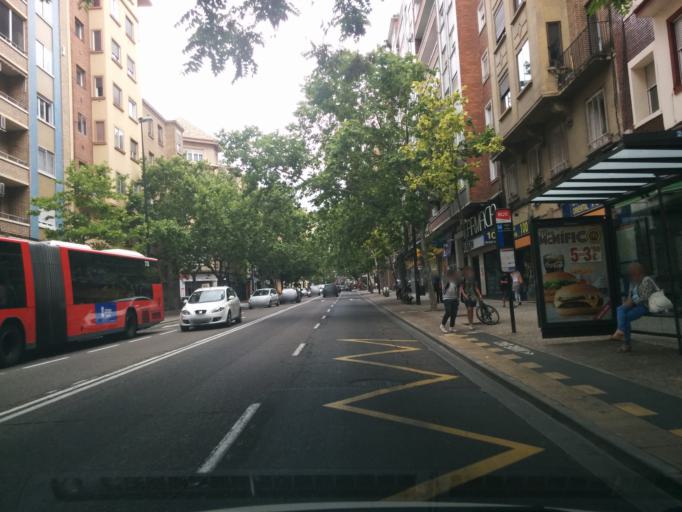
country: ES
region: Aragon
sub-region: Provincia de Zaragoza
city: Zaragoza
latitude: 41.6406
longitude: -0.8889
